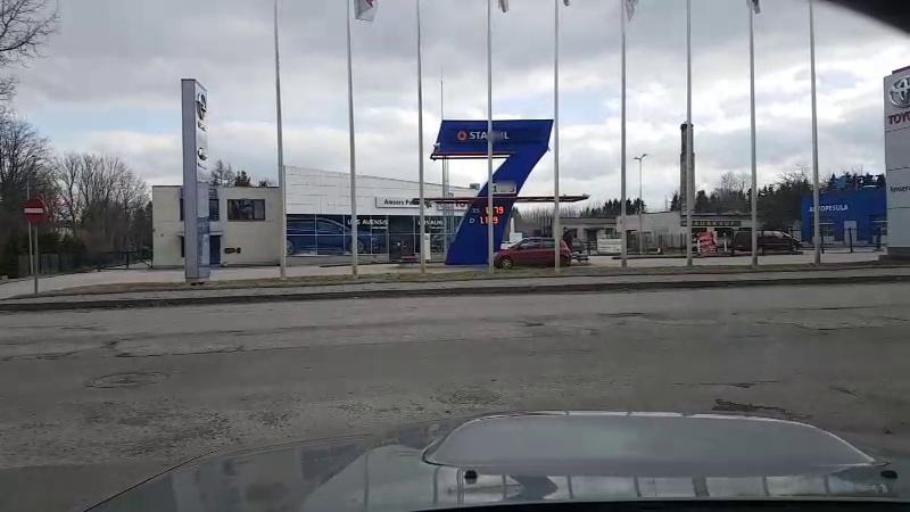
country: EE
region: Jaervamaa
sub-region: Paide linn
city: Paide
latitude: 58.8823
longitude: 25.5378
